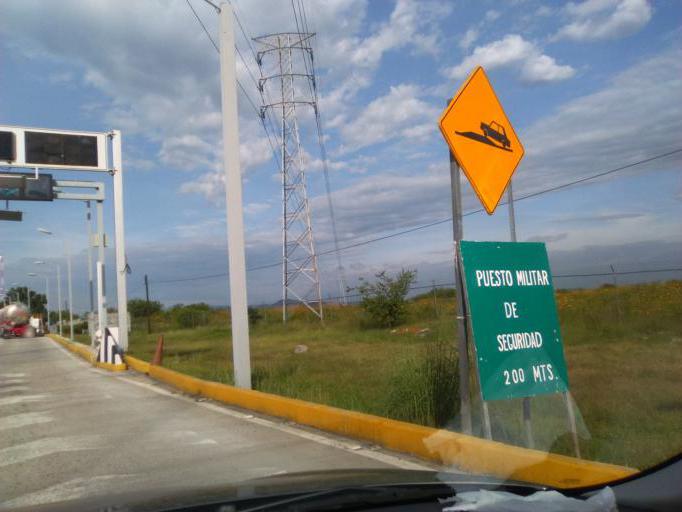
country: MX
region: Morelos
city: Ahuehuetzingo
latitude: 18.6962
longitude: -99.2794
